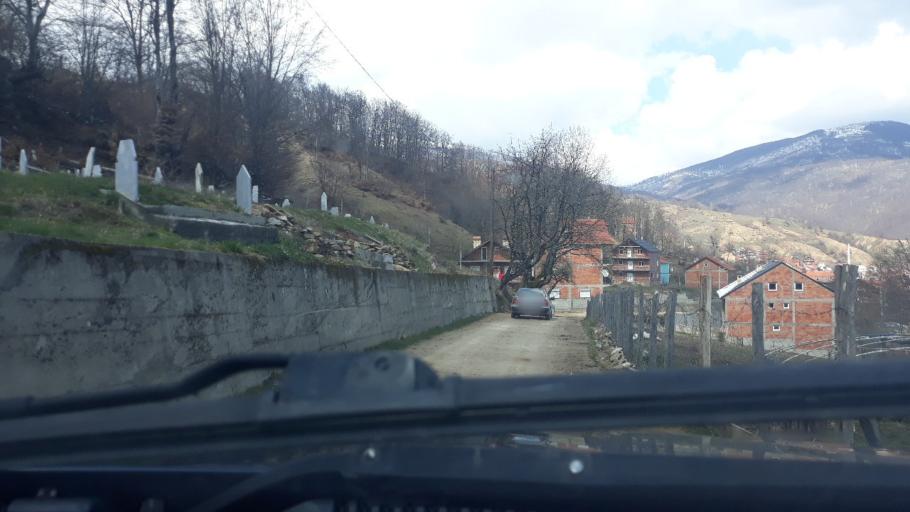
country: MK
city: Bogomila
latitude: 41.7181
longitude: 21.4832
